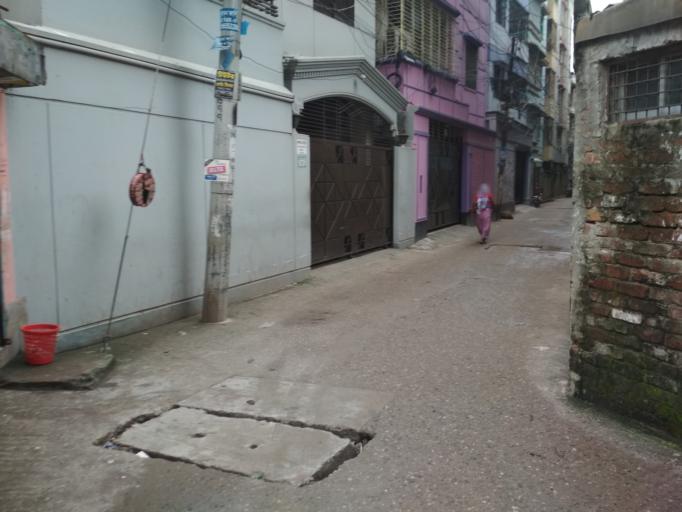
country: BD
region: Dhaka
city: Azimpur
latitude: 23.8041
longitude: 90.3683
